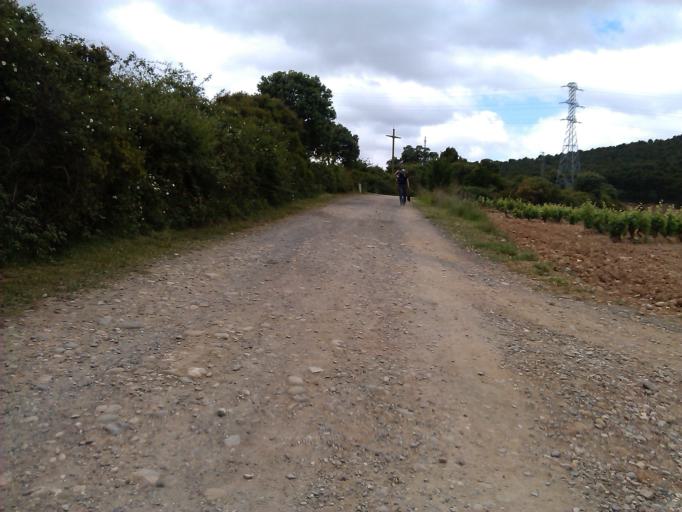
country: ES
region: La Rioja
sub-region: Provincia de La Rioja
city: Navarrete
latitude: 42.4393
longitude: -2.5218
